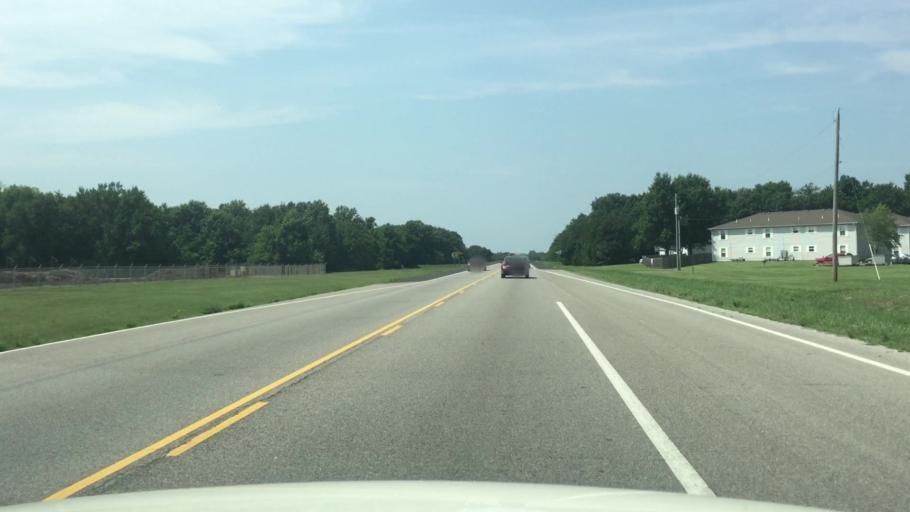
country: US
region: Kansas
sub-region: Crawford County
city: Pittsburg
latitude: 37.3872
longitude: -94.7109
